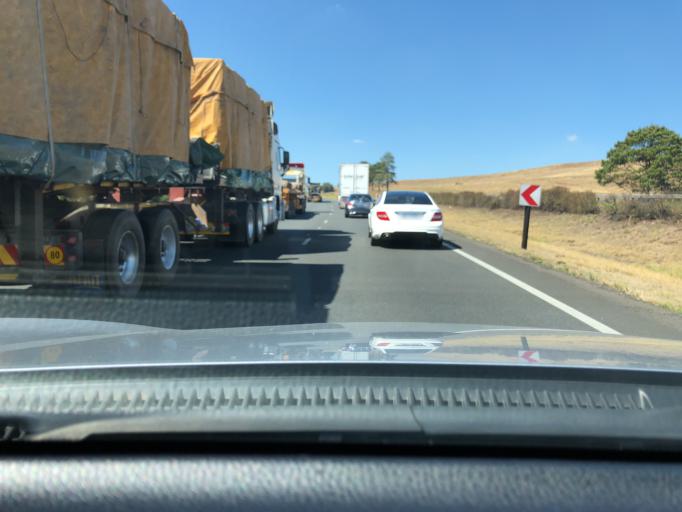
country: ZA
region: KwaZulu-Natal
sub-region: uMgungundlovu District Municipality
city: Mooirivier
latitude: -29.1105
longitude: 29.9422
